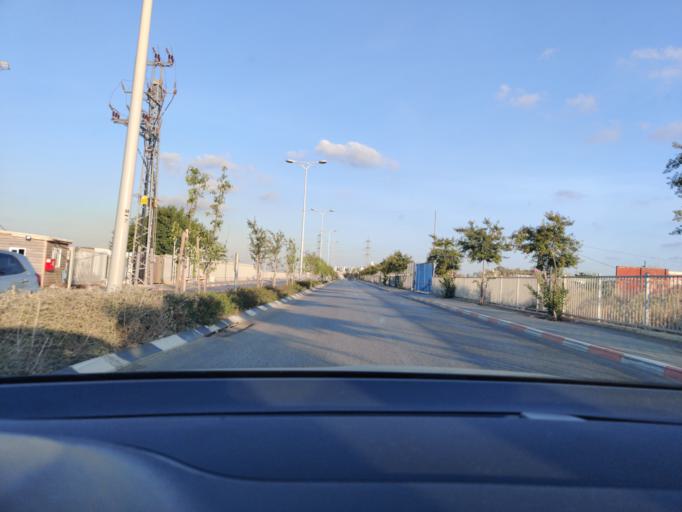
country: IL
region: Haifa
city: Hadera
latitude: 32.4421
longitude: 34.9345
